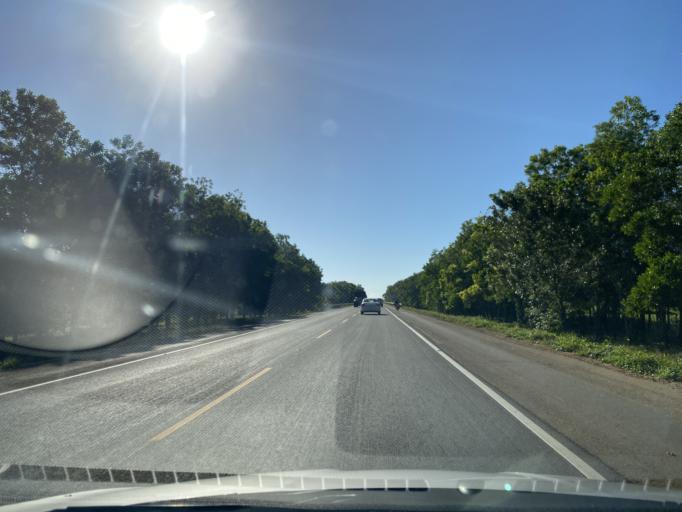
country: DO
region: Santo Domingo
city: Guerra
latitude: 18.5402
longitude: -69.7575
